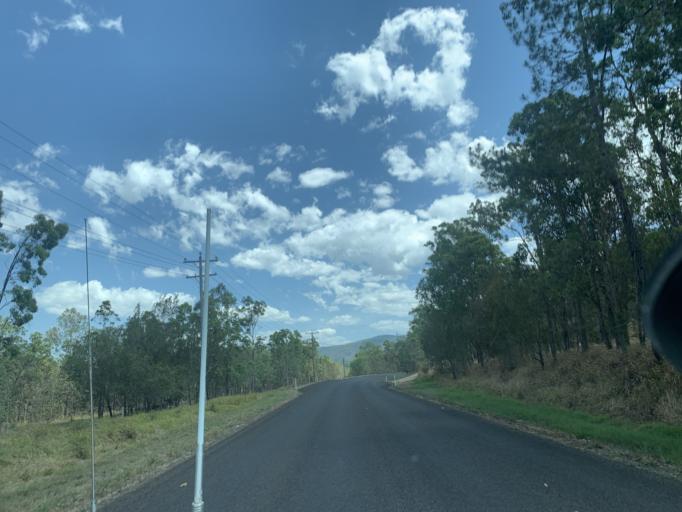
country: AU
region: Queensland
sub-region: Tablelands
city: Atherton
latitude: -17.2973
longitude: 145.4727
